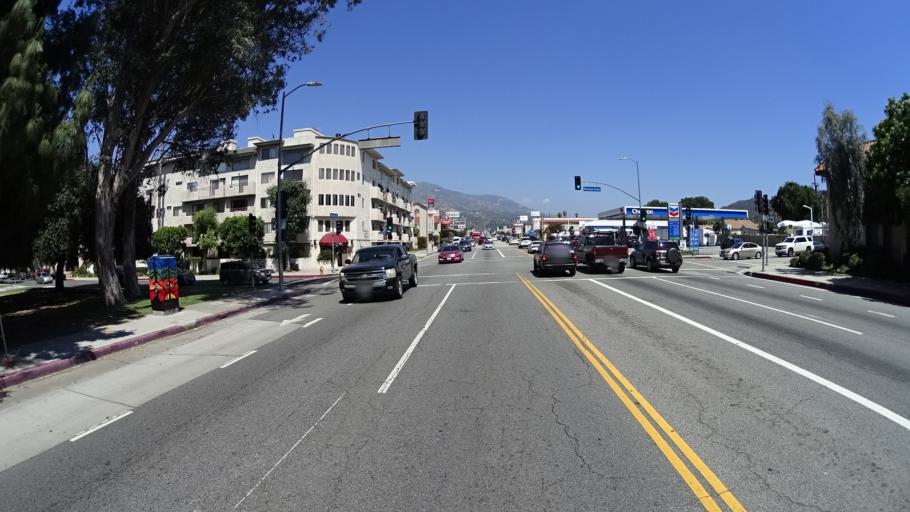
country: US
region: California
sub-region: Los Angeles County
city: Burbank
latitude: 34.2597
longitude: -118.3204
